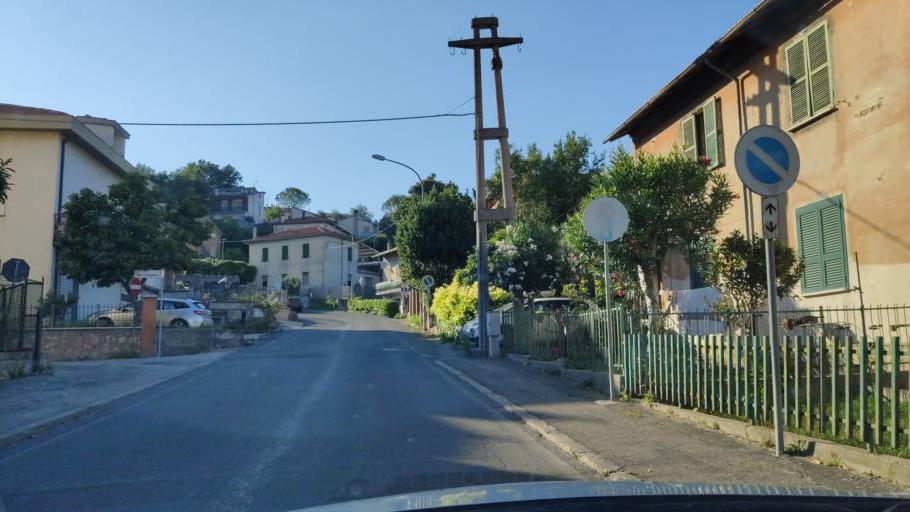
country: IT
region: Umbria
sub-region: Provincia di Terni
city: Narni Scalo
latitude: 42.5393
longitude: 12.5188
